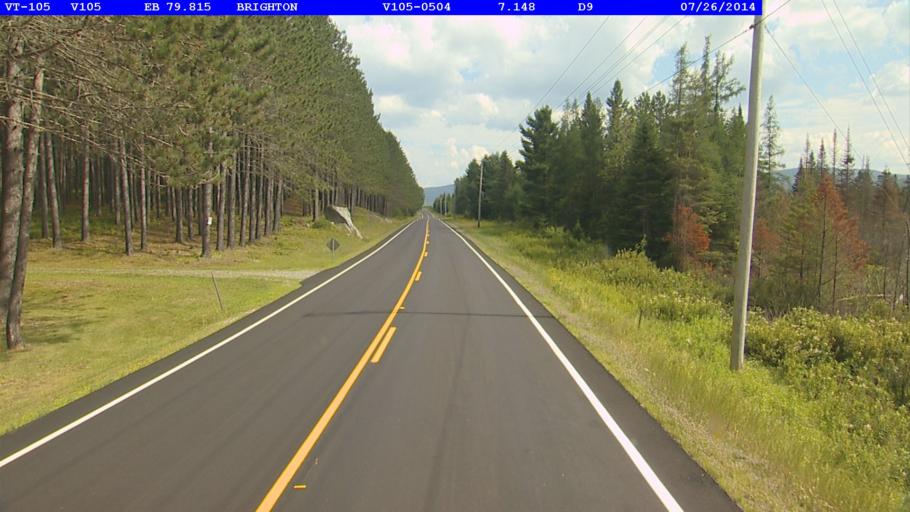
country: US
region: Vermont
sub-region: Caledonia County
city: Lyndonville
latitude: 44.7968
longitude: -71.8389
